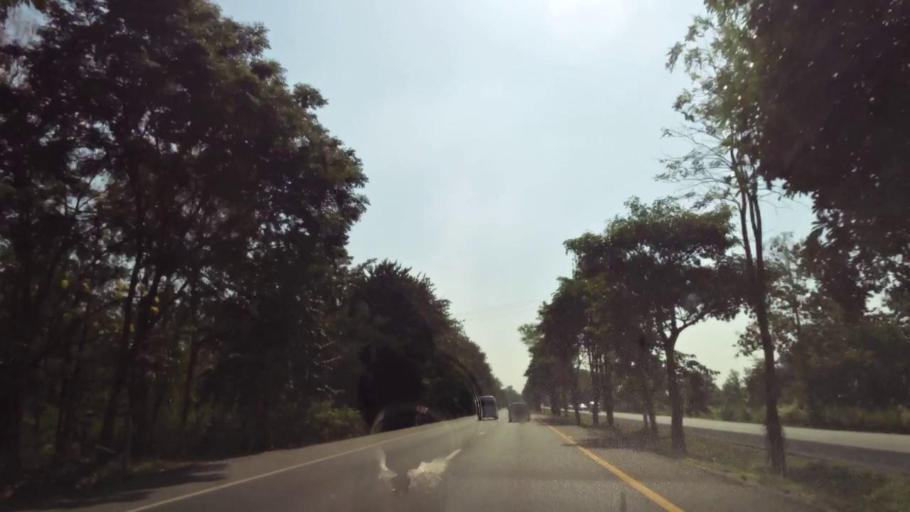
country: TH
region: Phichit
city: Bueng Na Rang
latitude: 16.0699
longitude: 100.1238
